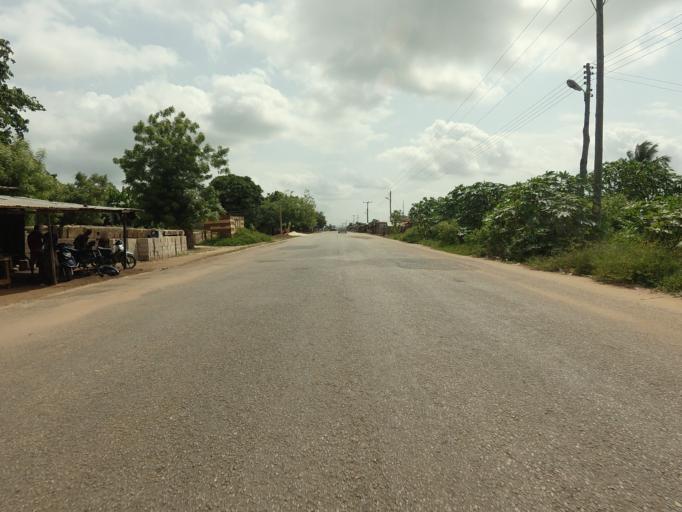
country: TG
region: Maritime
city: Lome
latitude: 6.2211
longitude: 1.0412
